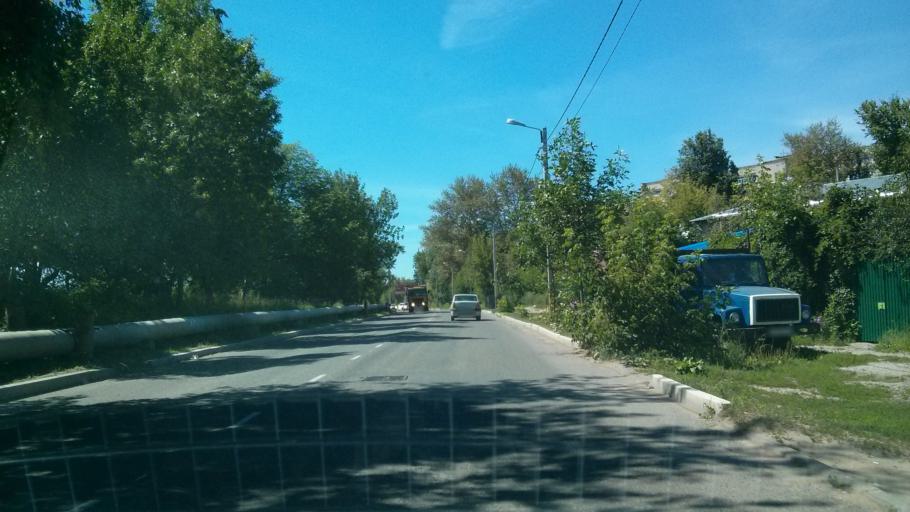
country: RU
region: Vladimir
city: Murom
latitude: 55.5658
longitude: 42.0511
